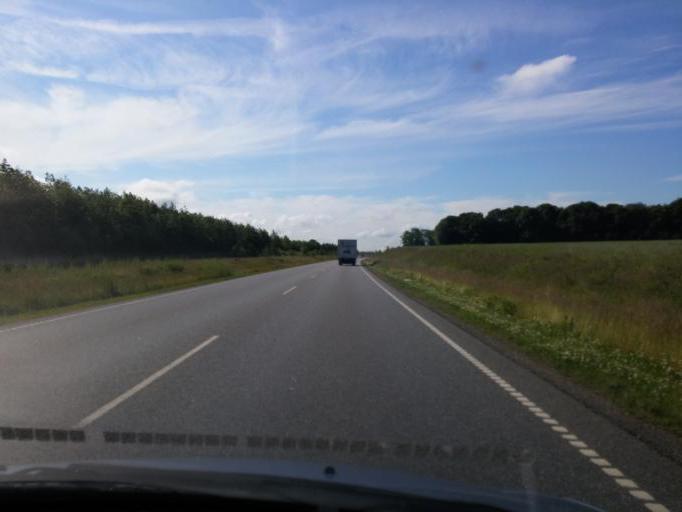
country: DK
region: South Denmark
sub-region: Odense Kommune
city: Bullerup
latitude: 55.4168
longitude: 10.4683
